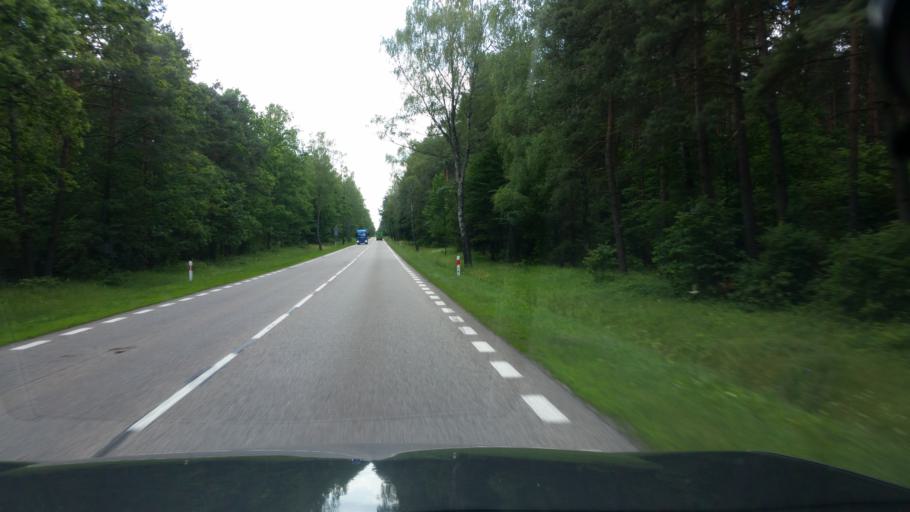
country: PL
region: Podlasie
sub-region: Powiat kolnenski
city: Stawiski
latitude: 53.3486
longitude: 22.1593
